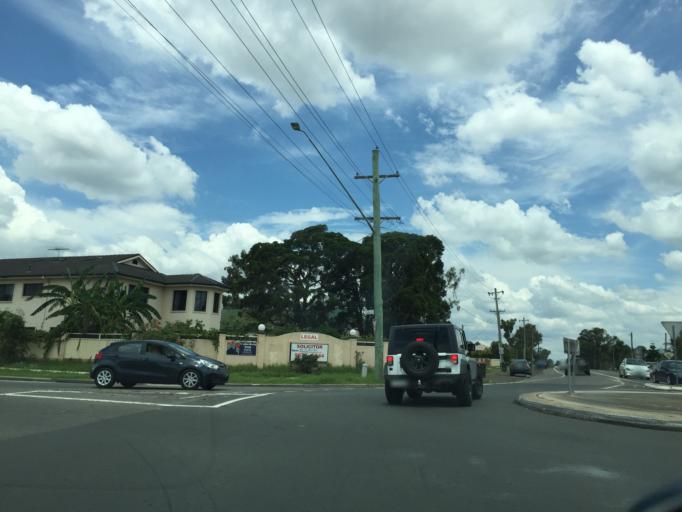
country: AU
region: New South Wales
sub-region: Blacktown
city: Glendenning
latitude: -33.7443
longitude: 150.8428
